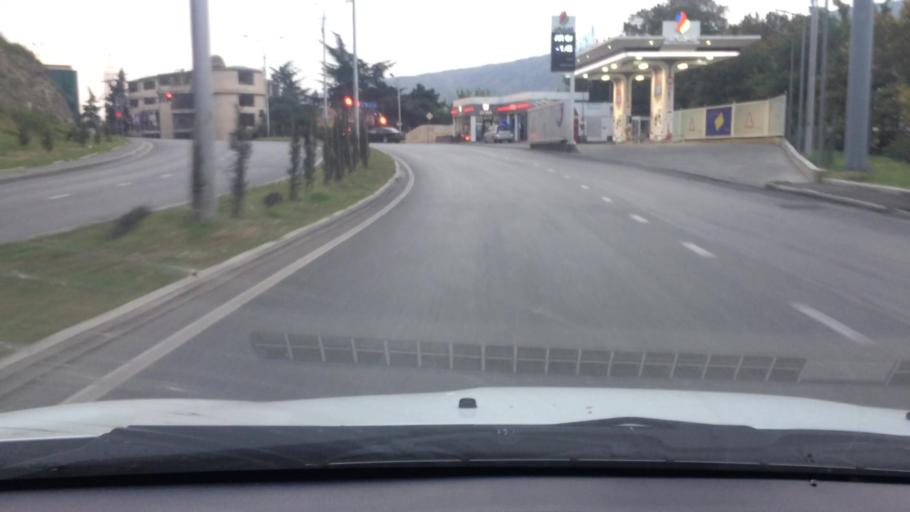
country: GE
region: T'bilisi
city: Tbilisi
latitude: 41.6849
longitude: 44.8237
